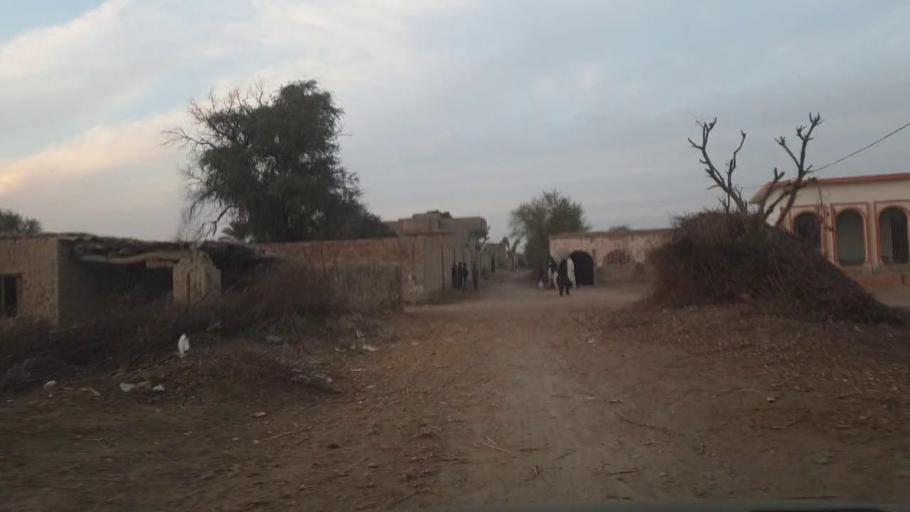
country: PK
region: Sindh
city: Shahpur Chakar
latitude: 26.0691
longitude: 68.5361
